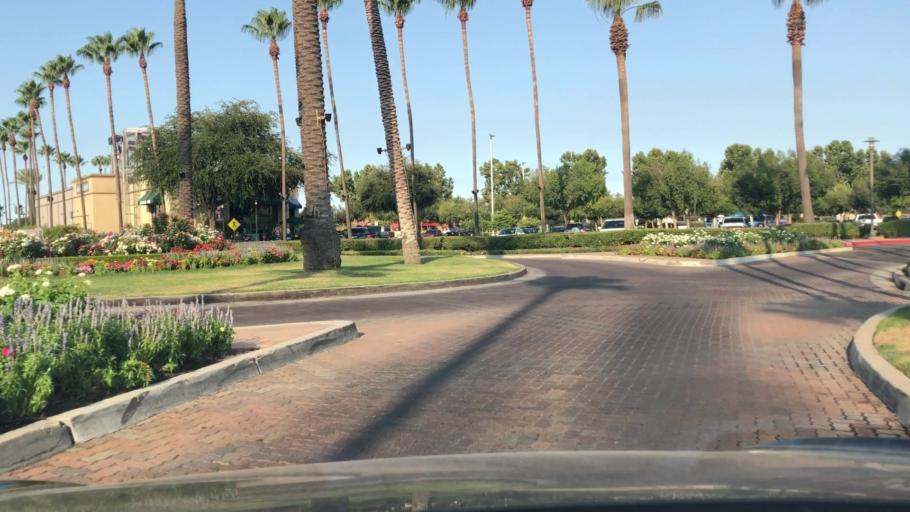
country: US
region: California
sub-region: Fresno County
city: Clovis
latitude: 36.8474
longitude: -119.7886
